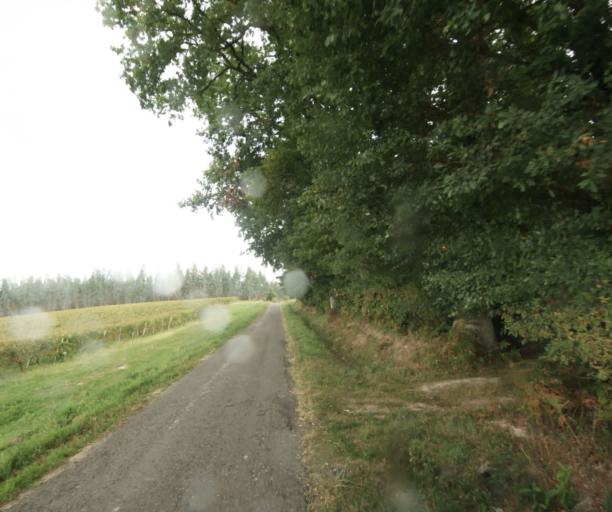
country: FR
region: Midi-Pyrenees
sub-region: Departement du Gers
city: Eauze
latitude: 43.8799
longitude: 0.0707
